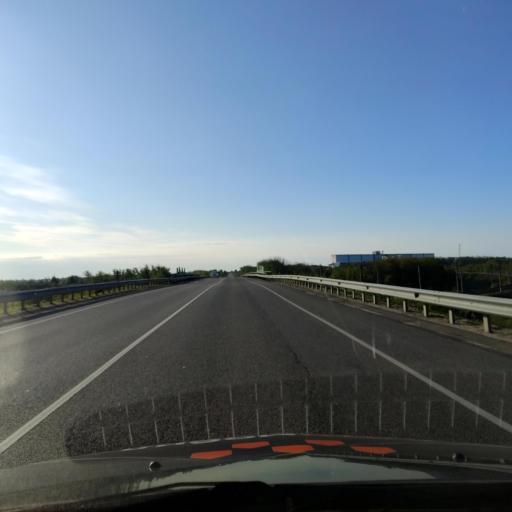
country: RU
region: Lipetsk
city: Yelets
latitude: 52.5639
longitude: 38.6779
